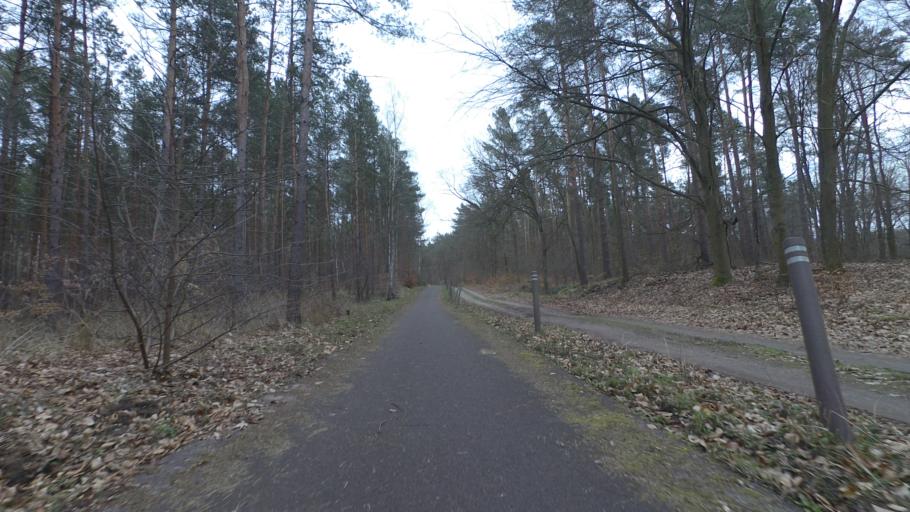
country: DE
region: Brandenburg
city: Lindow
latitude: 52.9932
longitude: 12.9120
